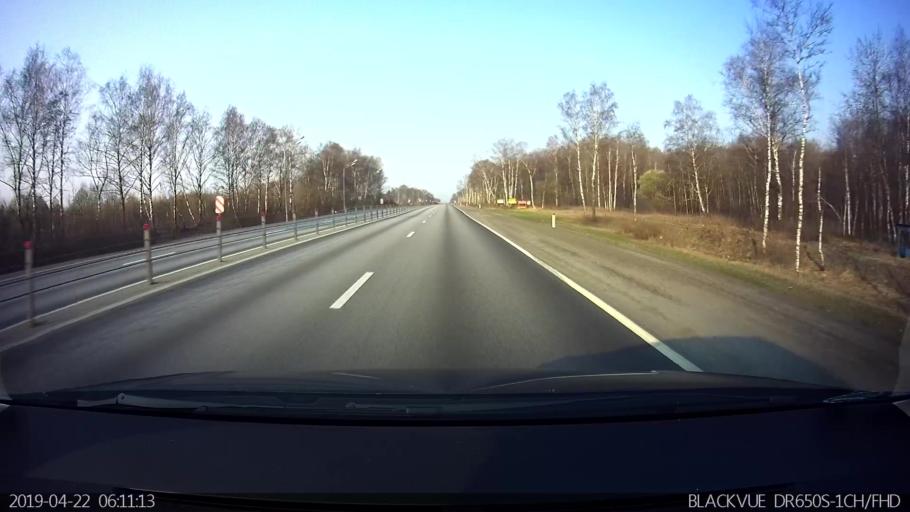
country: RU
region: Moskovskaya
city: Mozhaysk
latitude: 55.4883
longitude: 36.1557
